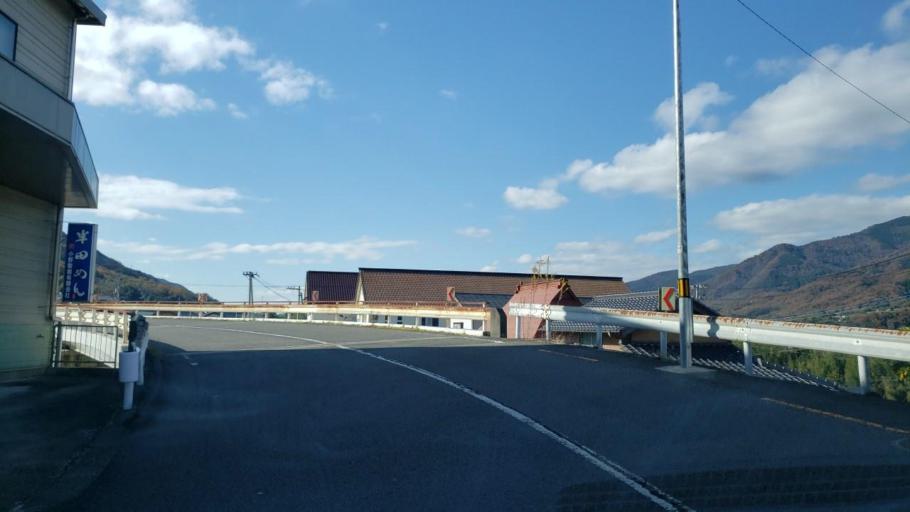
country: JP
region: Tokushima
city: Wakimachi
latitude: 34.0415
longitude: 134.0348
